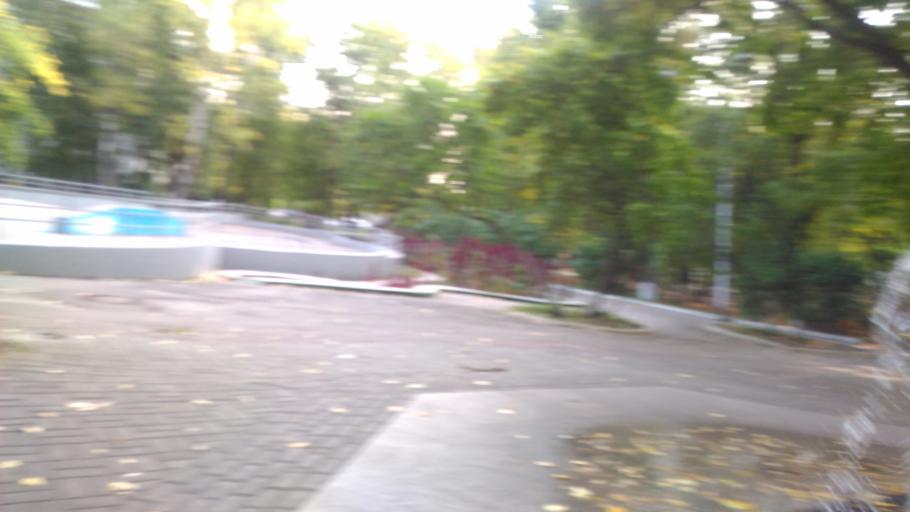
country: RU
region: Ulyanovsk
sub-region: Ulyanovskiy Rayon
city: Ulyanovsk
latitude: 54.3108
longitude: 48.3912
